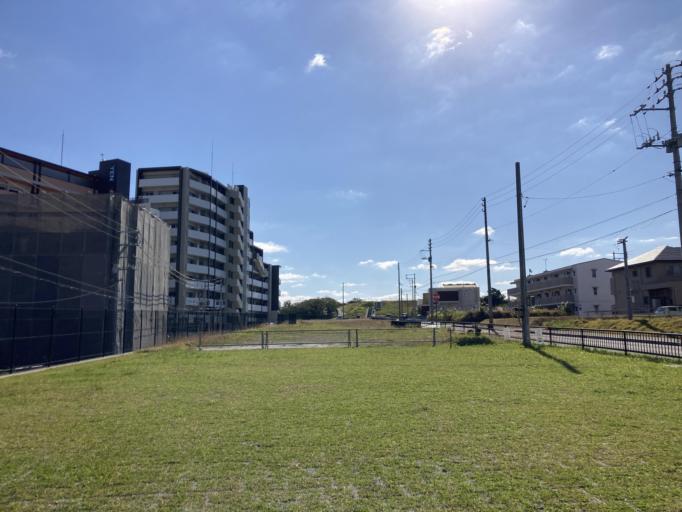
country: JP
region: Okinawa
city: Okinawa
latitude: 26.3116
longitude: 127.7968
